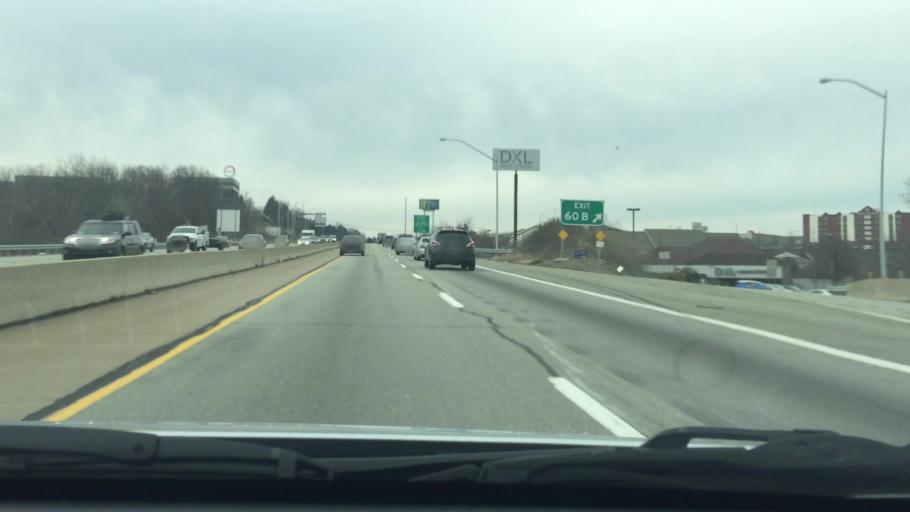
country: US
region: Pennsylvania
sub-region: Allegheny County
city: Rennerdale
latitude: 40.4417
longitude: -80.1581
